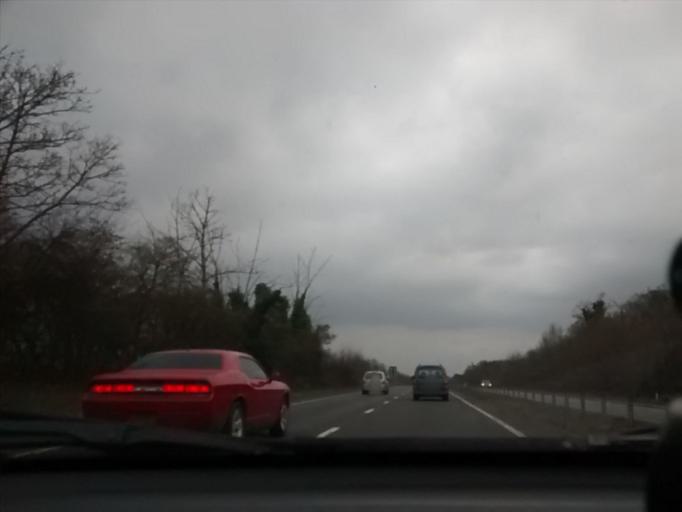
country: GB
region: England
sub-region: Cambridgeshire
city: Sawston
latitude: 52.1051
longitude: 0.2100
